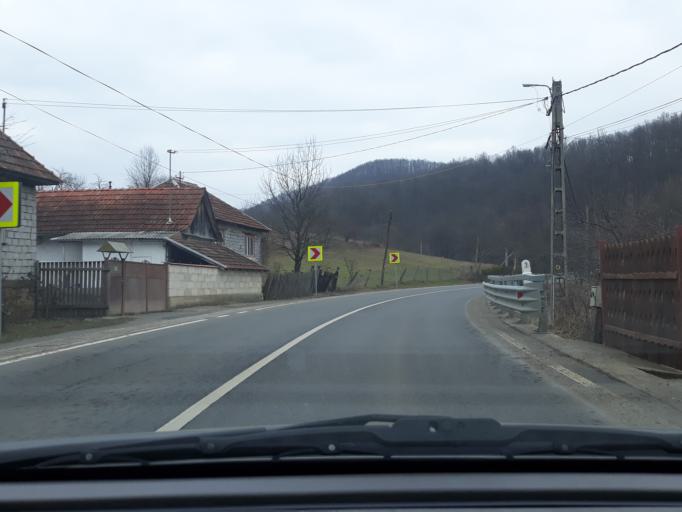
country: RO
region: Bihor
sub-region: Oras Alesd
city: Pestis
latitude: 47.0909
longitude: 22.4081
